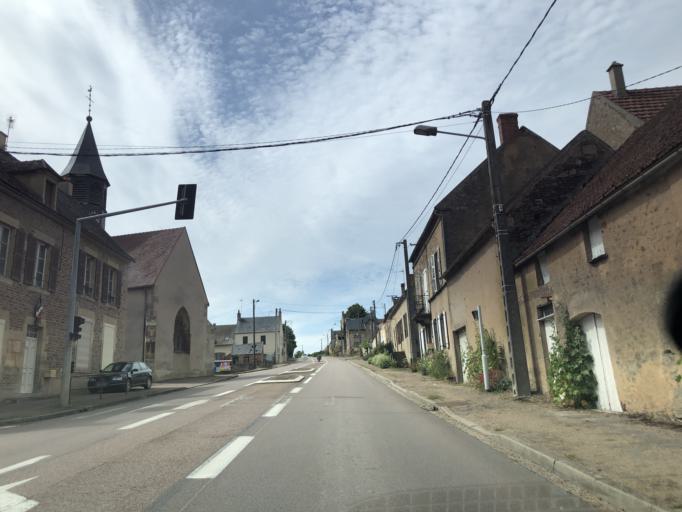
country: FR
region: Bourgogne
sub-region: Departement de l'Yonne
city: Avallon
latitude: 47.4501
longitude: 4.0750
